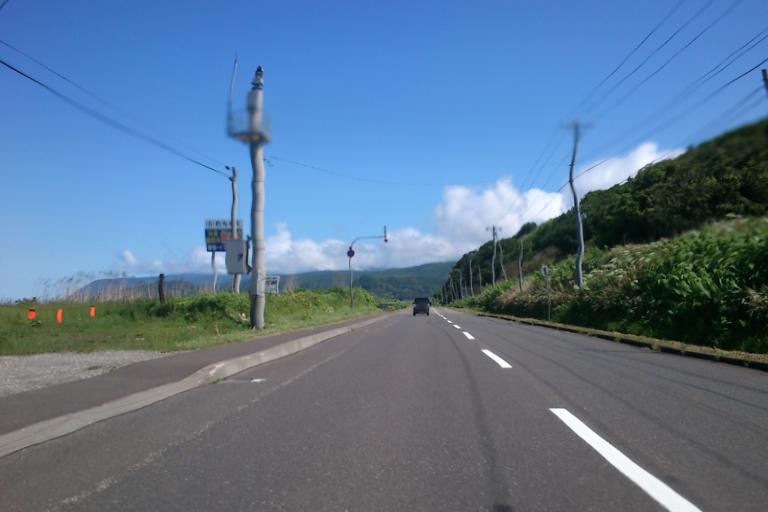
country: JP
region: Hokkaido
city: Ishikari
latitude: 43.5646
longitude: 141.3799
